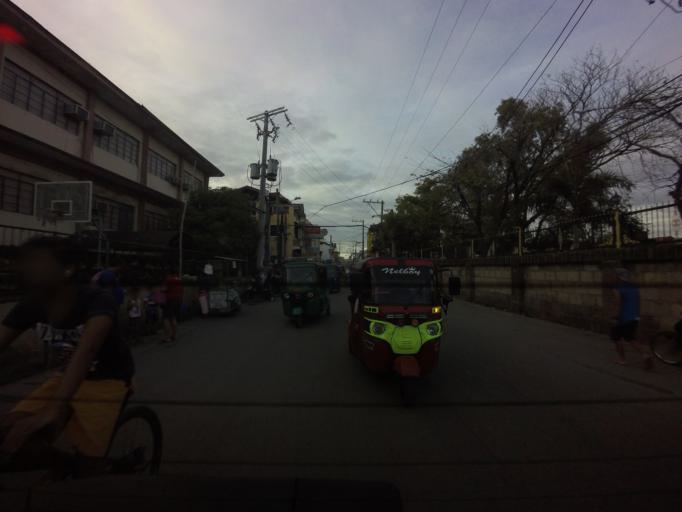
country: PH
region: Central Luzon
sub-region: Province of Bulacan
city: Obando
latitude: 14.7102
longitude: 120.9364
